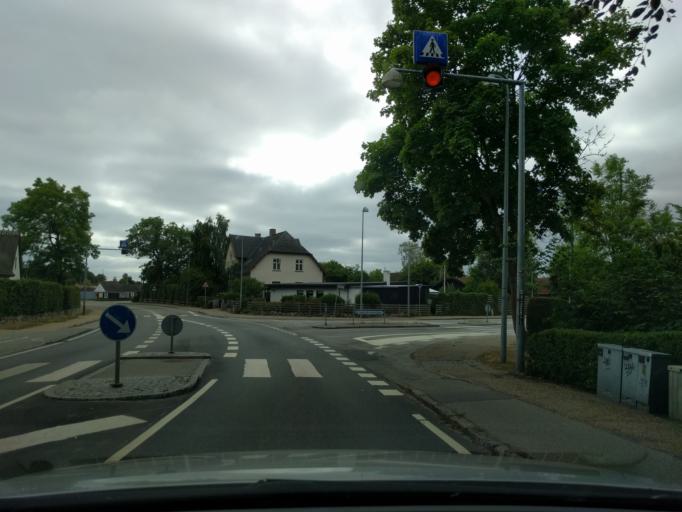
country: DK
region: Capital Region
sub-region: Helsingor Kommune
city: Espergaerde
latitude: 56.0002
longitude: 12.5352
